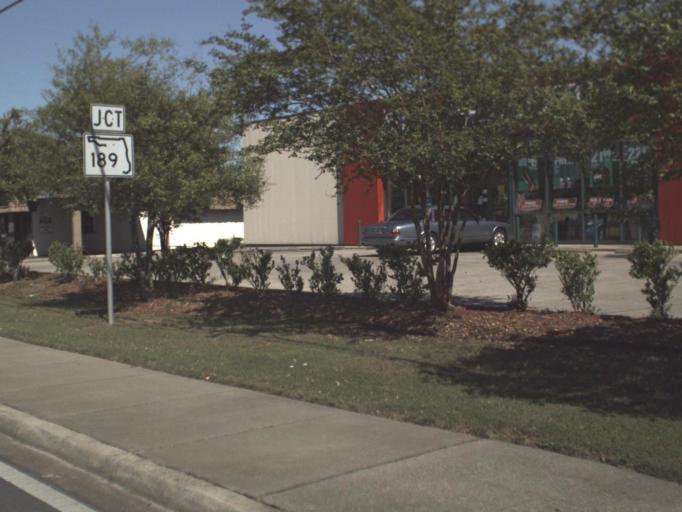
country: US
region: Florida
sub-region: Okaloosa County
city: Wright
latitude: 30.4271
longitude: -86.6400
